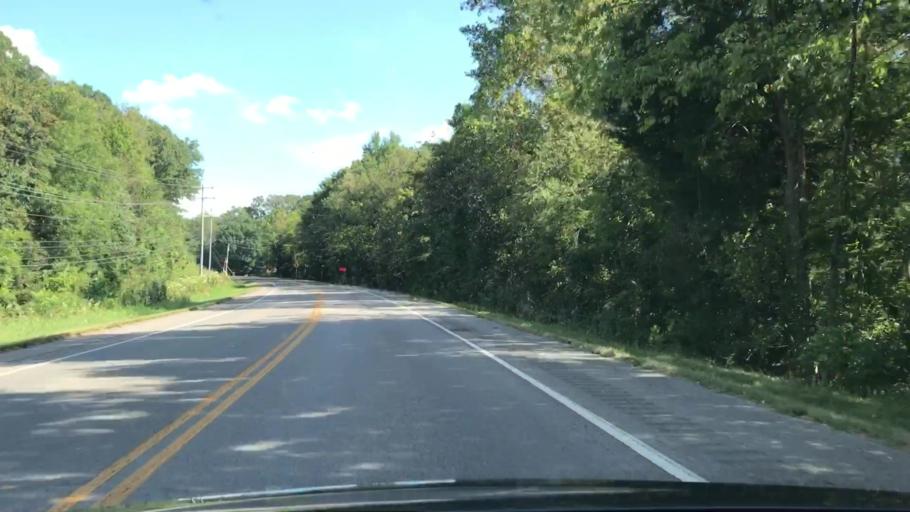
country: US
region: Alabama
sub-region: Limestone County
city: Ardmore
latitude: 35.0063
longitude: -86.8741
